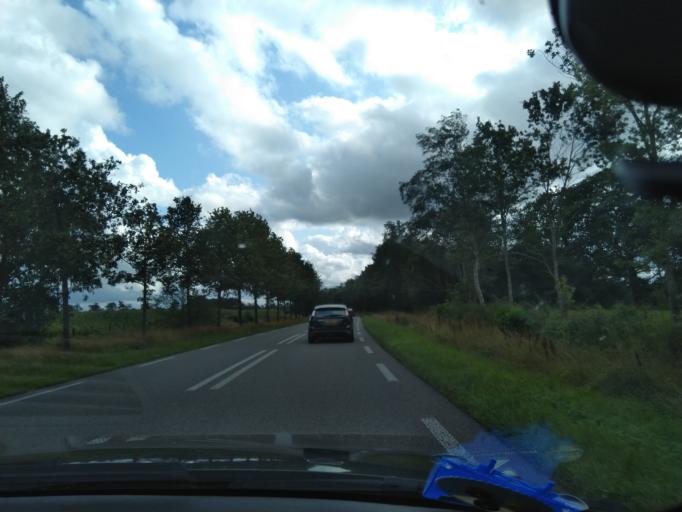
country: NL
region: Groningen
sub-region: Gemeente Leek
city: Leek
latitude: 53.1464
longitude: 6.4821
